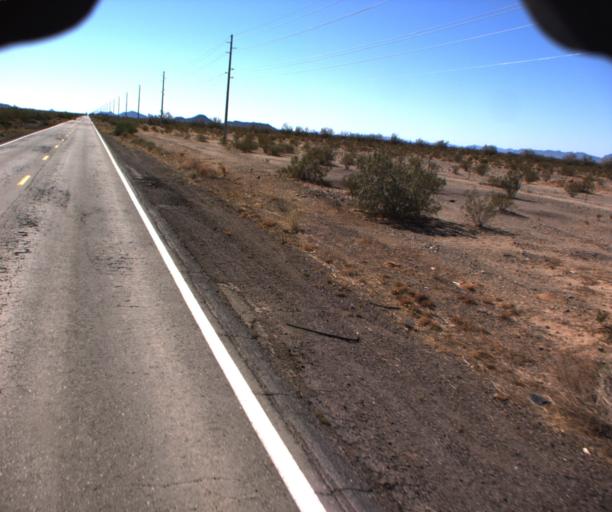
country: US
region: Arizona
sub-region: La Paz County
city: Salome
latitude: 33.8222
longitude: -113.8644
